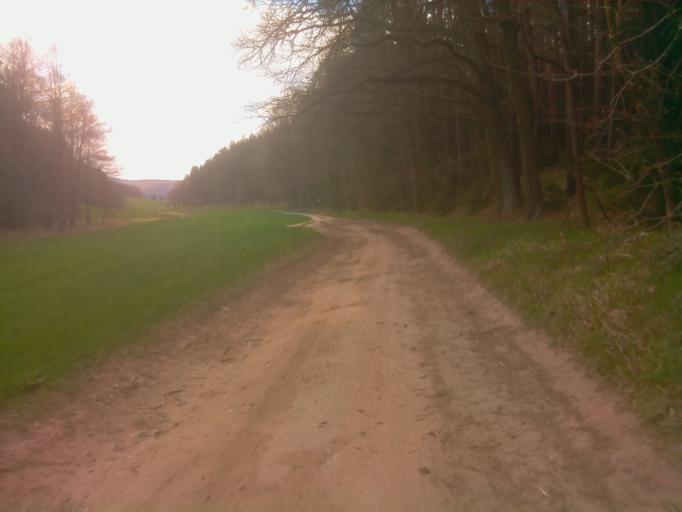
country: DE
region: Thuringia
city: Unterbodnitz
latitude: 50.8311
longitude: 11.6366
